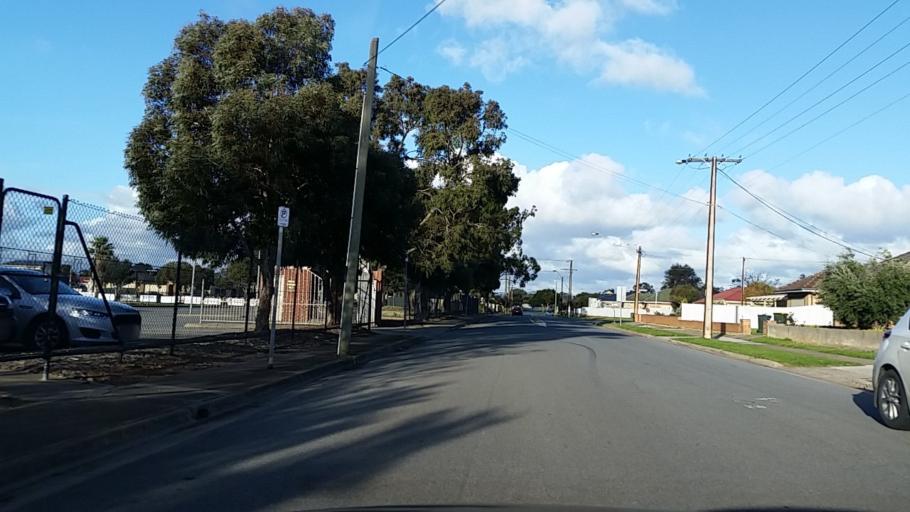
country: AU
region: South Australia
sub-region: Charles Sturt
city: Woodville West
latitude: -34.8879
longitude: 138.5214
